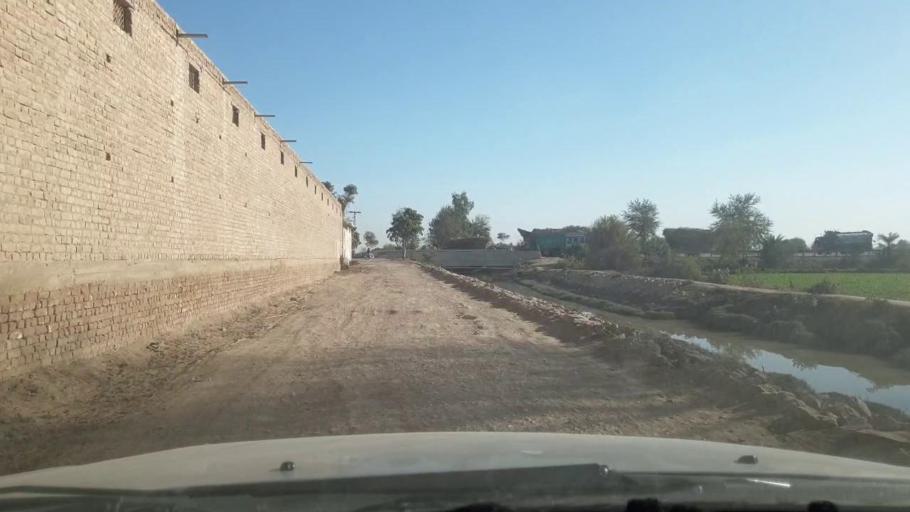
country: PK
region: Sindh
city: Adilpur
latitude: 27.9405
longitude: 69.2209
